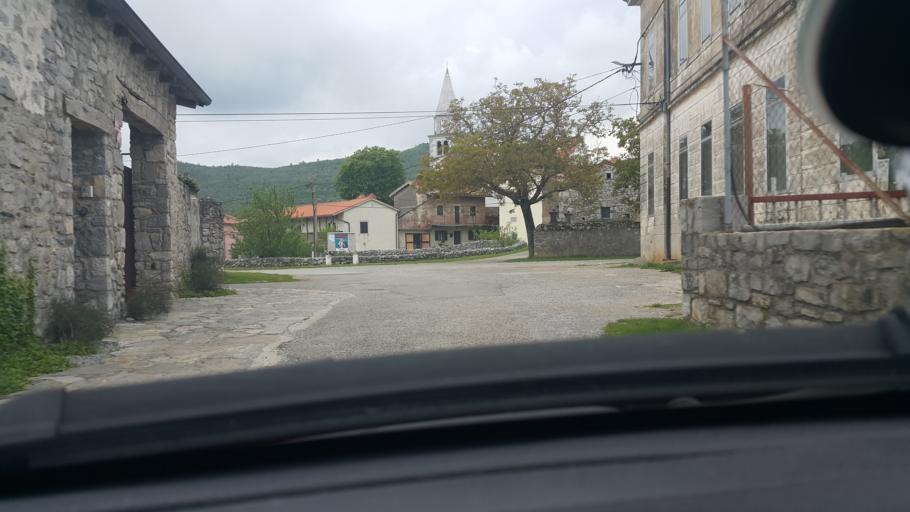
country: SI
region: Komen
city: Komen
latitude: 45.8419
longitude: 13.7354
